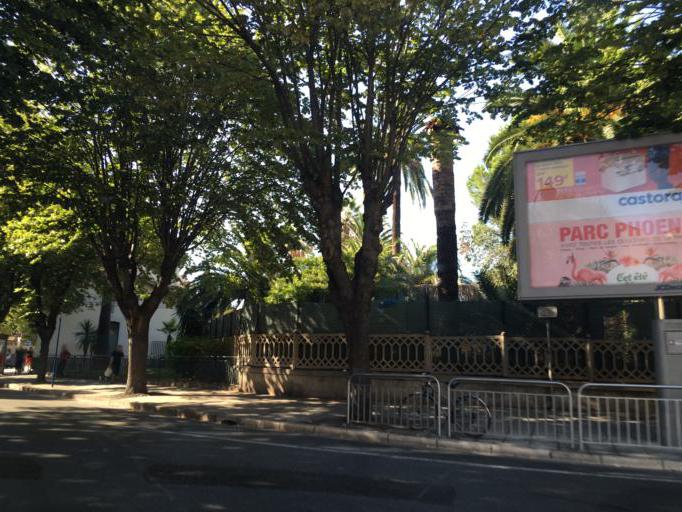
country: FR
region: Provence-Alpes-Cote d'Azur
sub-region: Departement des Alpes-Maritimes
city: Villefranche-sur-Mer
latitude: 43.7052
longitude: 7.2908
